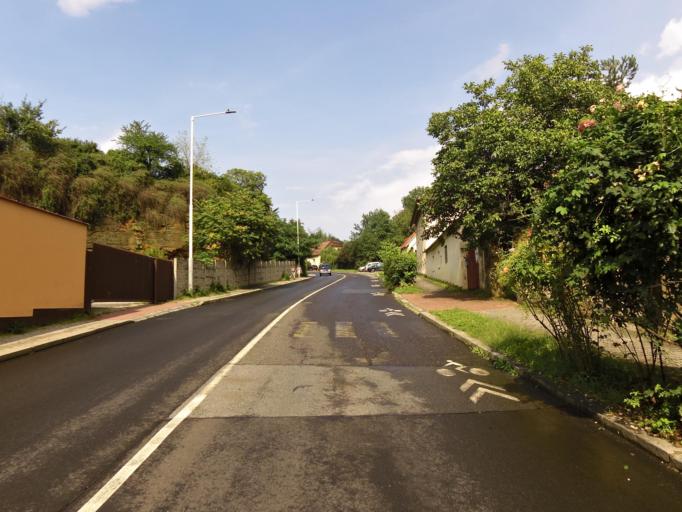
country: CZ
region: Praha
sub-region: Praha 8
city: Liben
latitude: 50.1212
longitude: 14.4717
